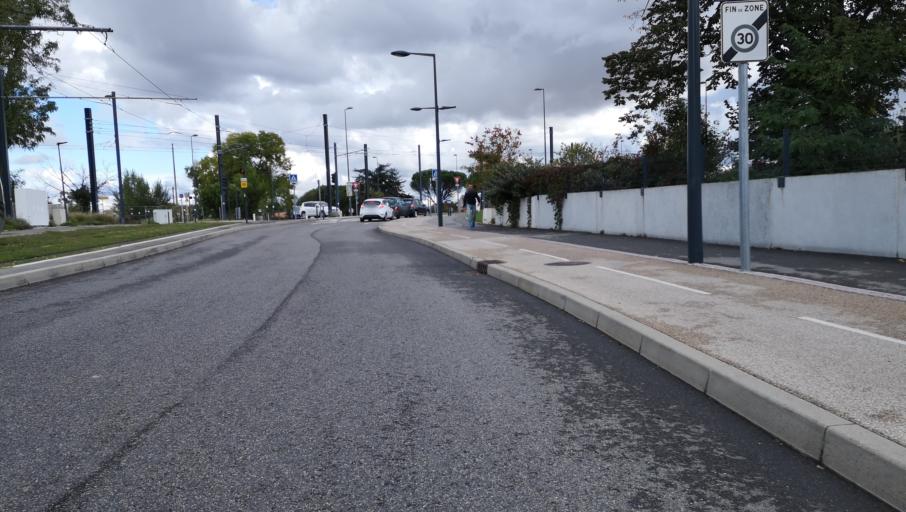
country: FR
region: Midi-Pyrenees
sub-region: Departement de la Haute-Garonne
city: Blagnac
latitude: 43.6217
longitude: 1.3956
